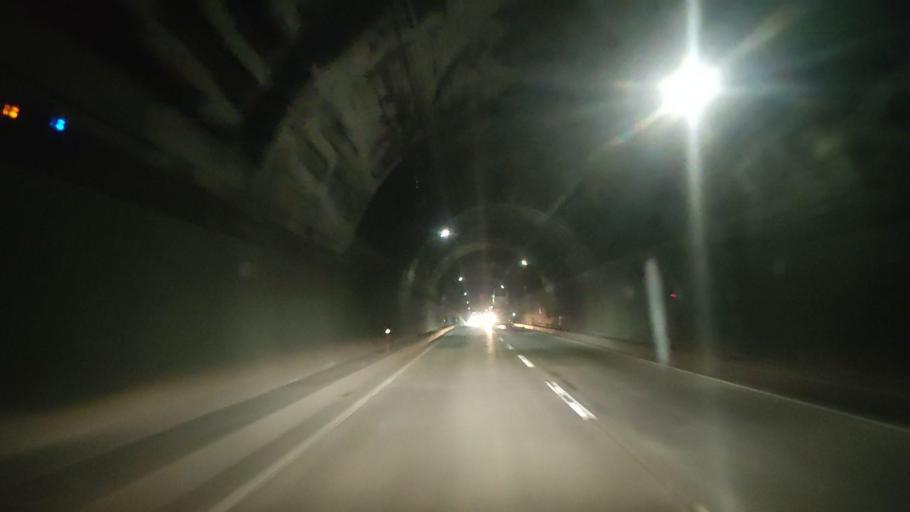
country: JP
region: Kagoshima
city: Okuchi-shinohara
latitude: 31.9751
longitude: 130.7413
